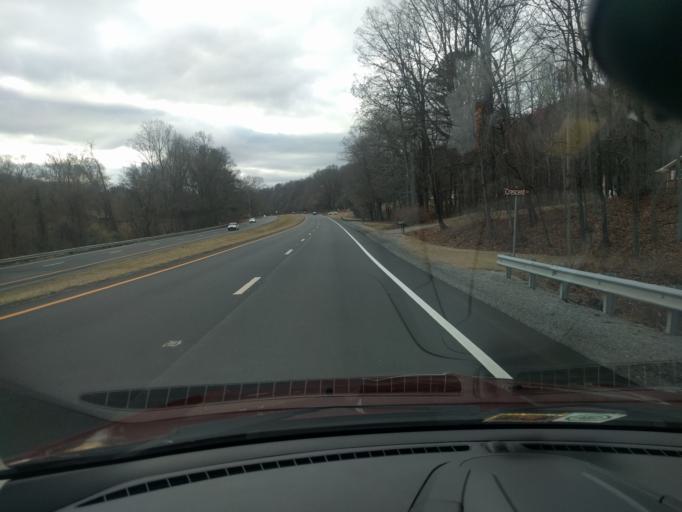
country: US
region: Virginia
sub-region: Botetourt County
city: Blue Ridge
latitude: 37.3960
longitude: -79.7733
